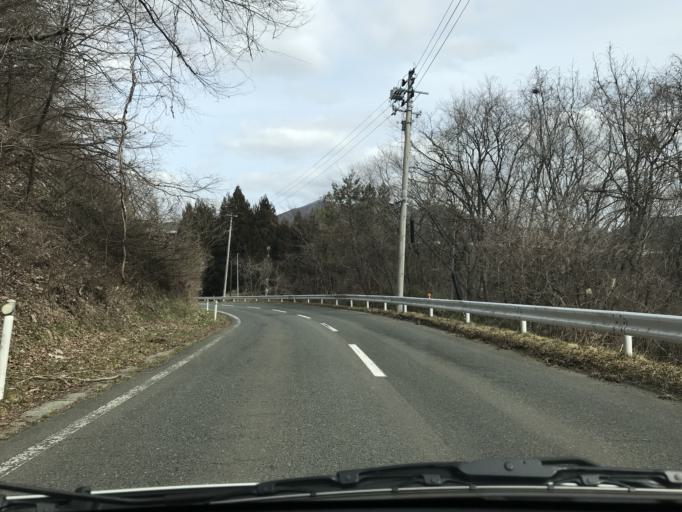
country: JP
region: Iwate
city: Kitakami
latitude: 39.2875
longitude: 141.3228
